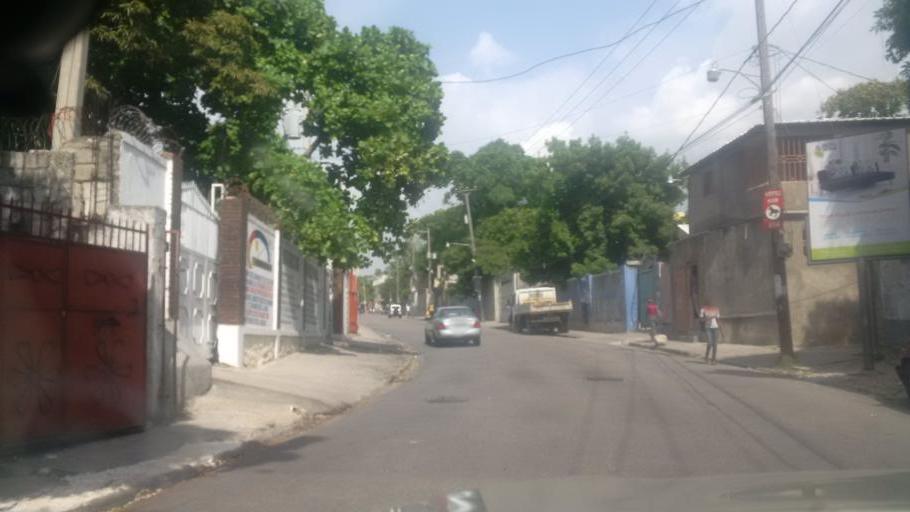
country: HT
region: Ouest
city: Port-au-Prince
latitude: 18.5343
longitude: -72.3235
